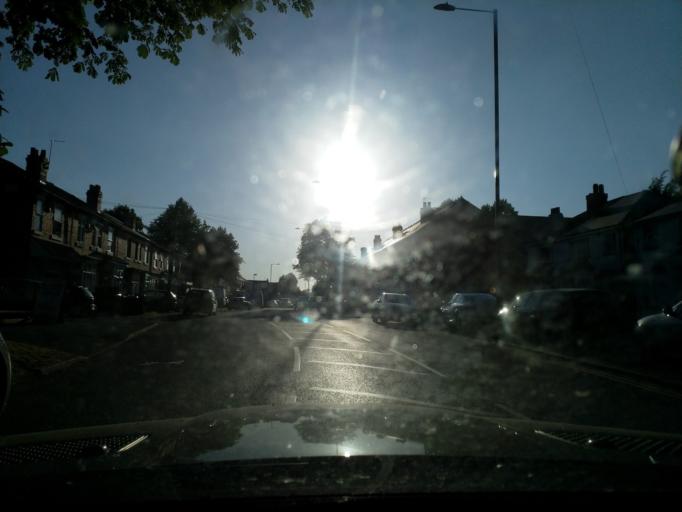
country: GB
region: England
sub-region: City and Borough of Birmingham
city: Acocks Green
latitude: 52.4425
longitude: -1.8458
